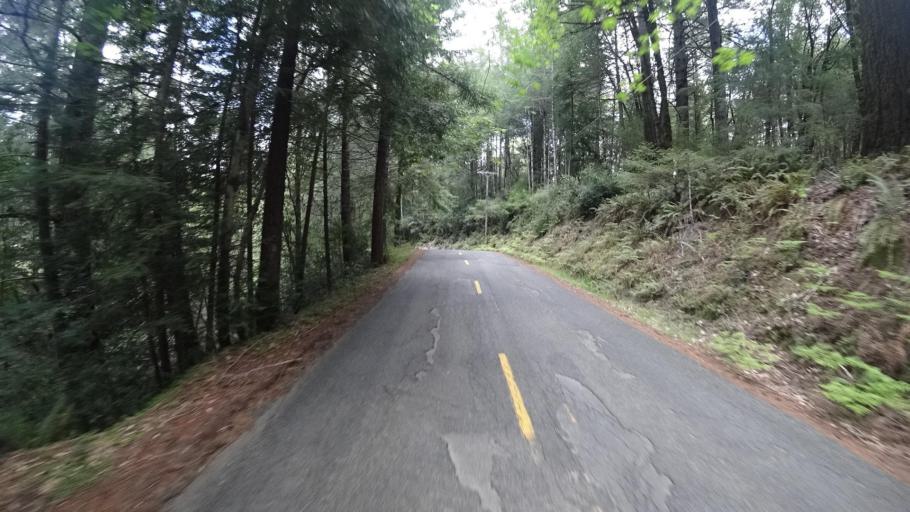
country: US
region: California
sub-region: Humboldt County
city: Redway
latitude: 40.0018
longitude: -123.9282
